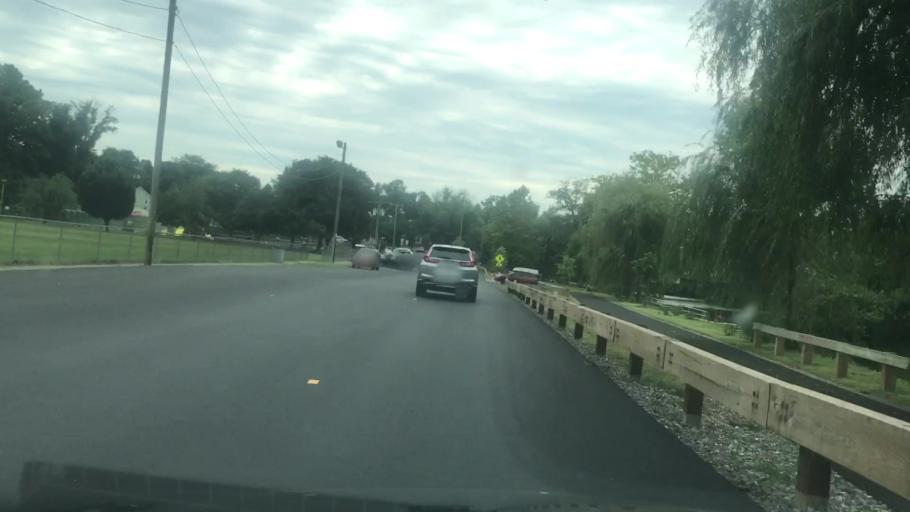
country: US
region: Connecticut
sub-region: Litchfield County
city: New Milford
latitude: 41.5773
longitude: -73.4154
